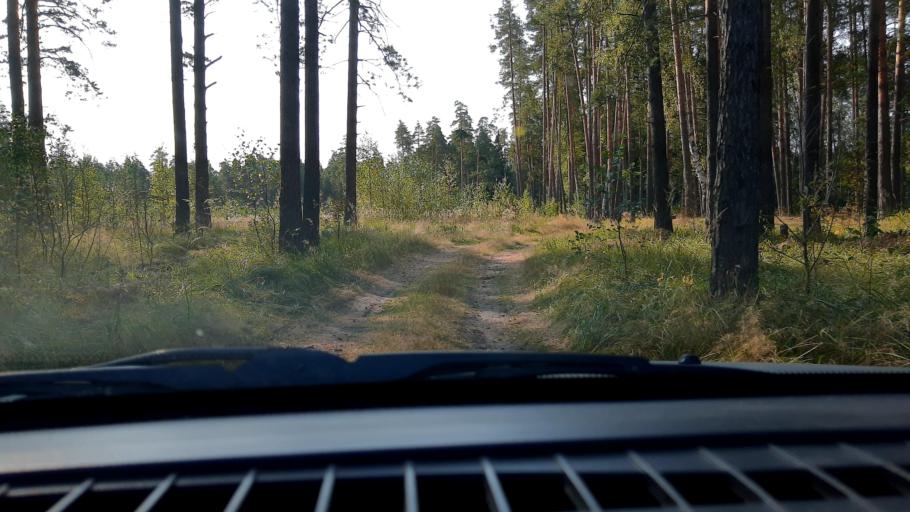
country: RU
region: Nizjnij Novgorod
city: Lukino
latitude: 56.4069
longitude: 43.6329
